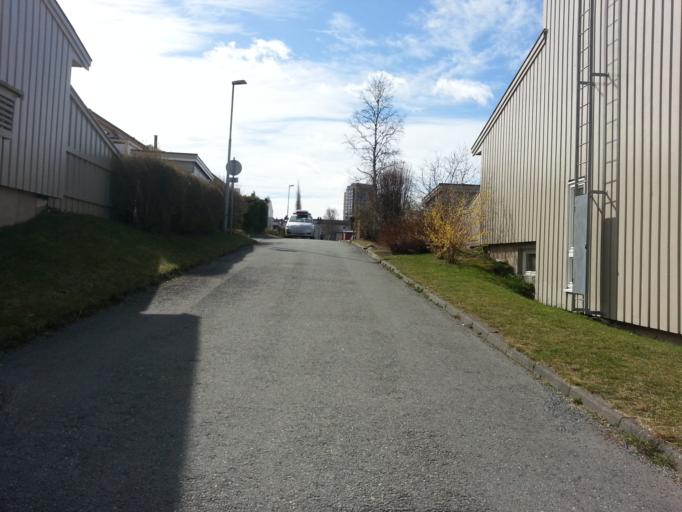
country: NO
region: Sor-Trondelag
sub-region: Trondheim
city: Trondheim
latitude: 63.4275
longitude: 10.4492
